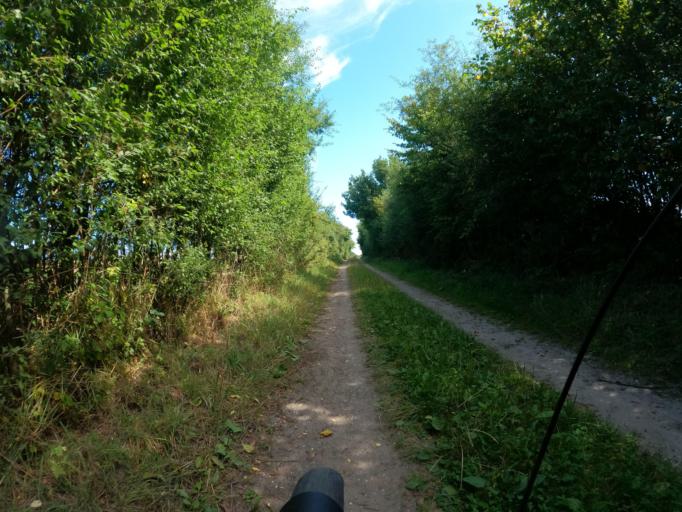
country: DE
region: Schleswig-Holstein
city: Dollerup
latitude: 54.7815
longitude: 9.7140
